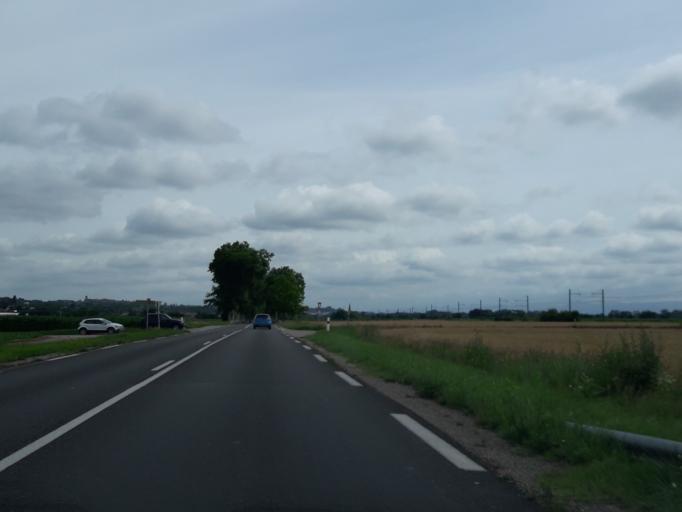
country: FR
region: Rhone-Alpes
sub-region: Departement de l'Ain
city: Perouges
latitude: 45.8765
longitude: 5.1605
